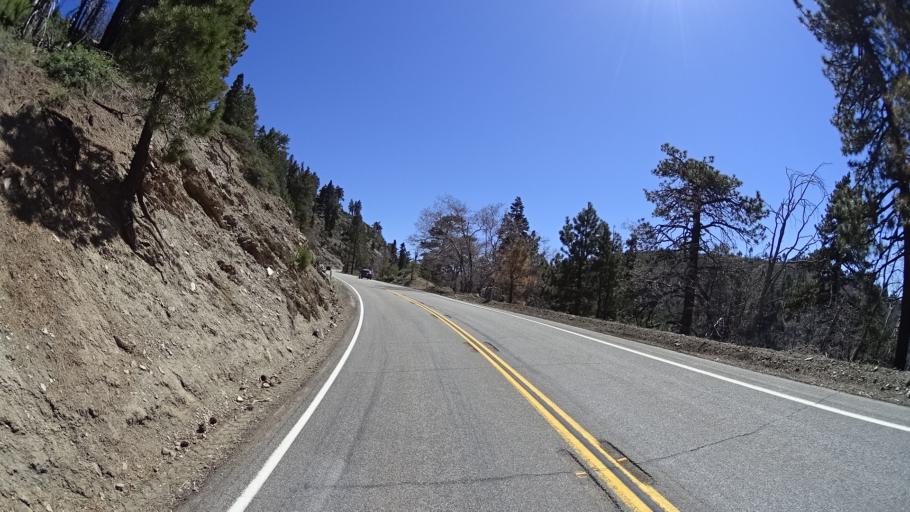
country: US
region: California
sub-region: San Bernardino County
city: Wrightwood
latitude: 34.3781
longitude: -117.7058
